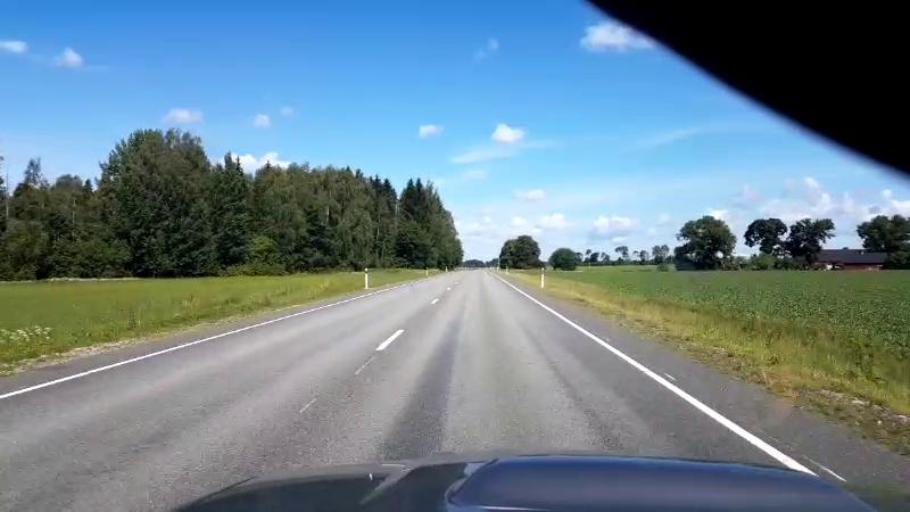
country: EE
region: Jaervamaa
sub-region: Jaerva-Jaani vald
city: Jarva-Jaani
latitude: 59.1633
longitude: 25.7609
